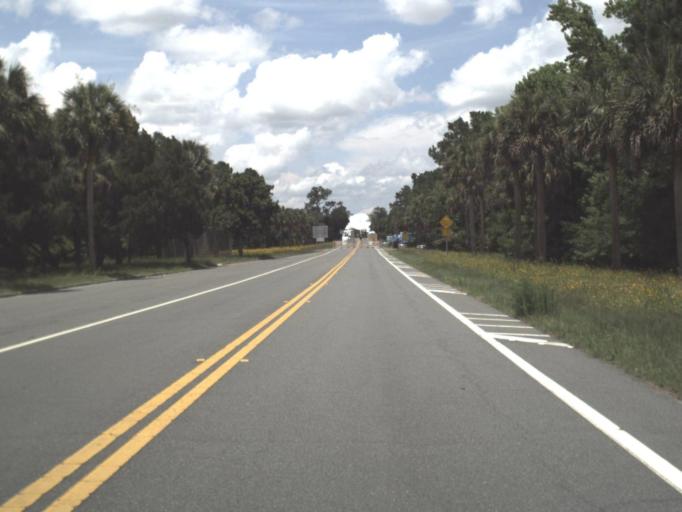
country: US
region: Georgia
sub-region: Camden County
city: Kingsland
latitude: 30.7378
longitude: -81.6881
